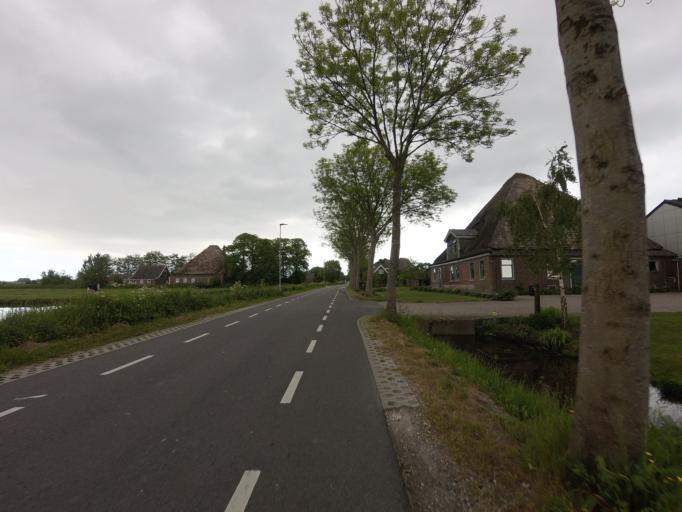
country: NL
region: North Holland
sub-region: Gemeente Hoorn
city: Hoorn
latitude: 52.6555
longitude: 5.0201
